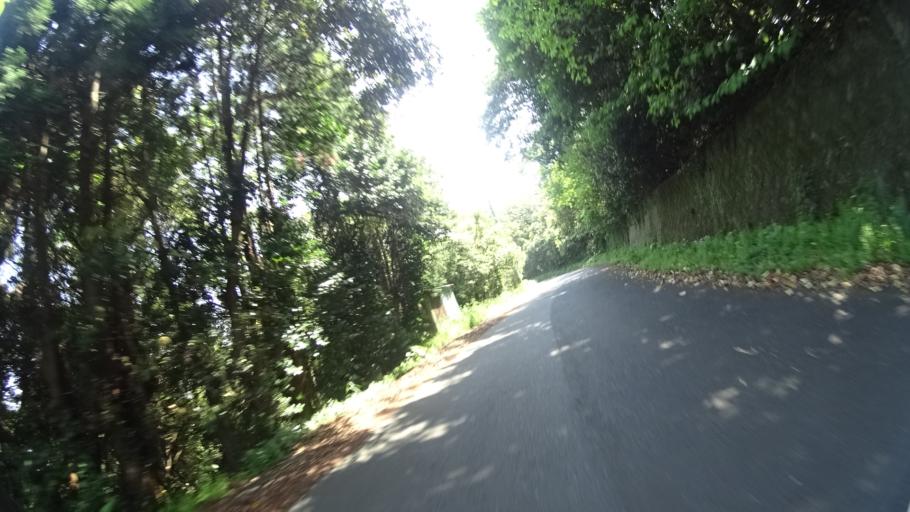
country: JP
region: Ehime
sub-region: Nishiuwa-gun
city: Ikata-cho
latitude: 33.3774
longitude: 132.0623
